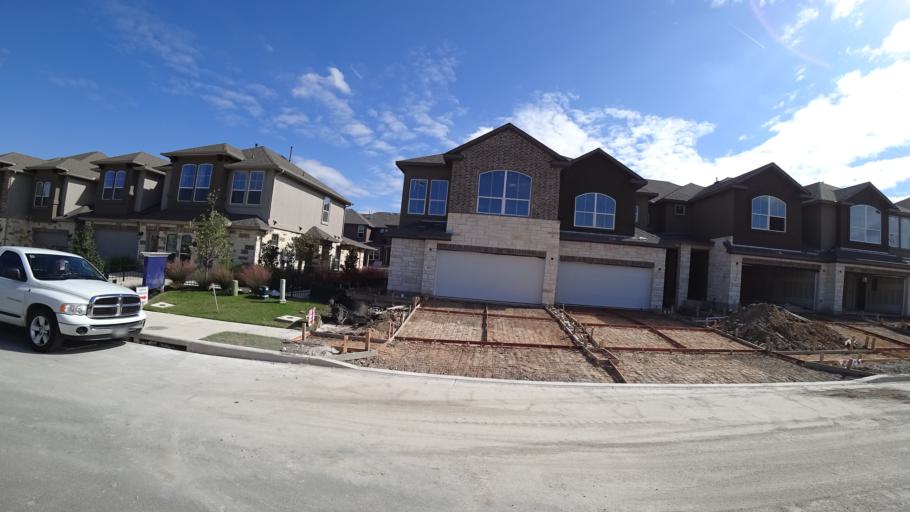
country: US
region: Texas
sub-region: Travis County
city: Windemere
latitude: 30.4508
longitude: -97.6363
